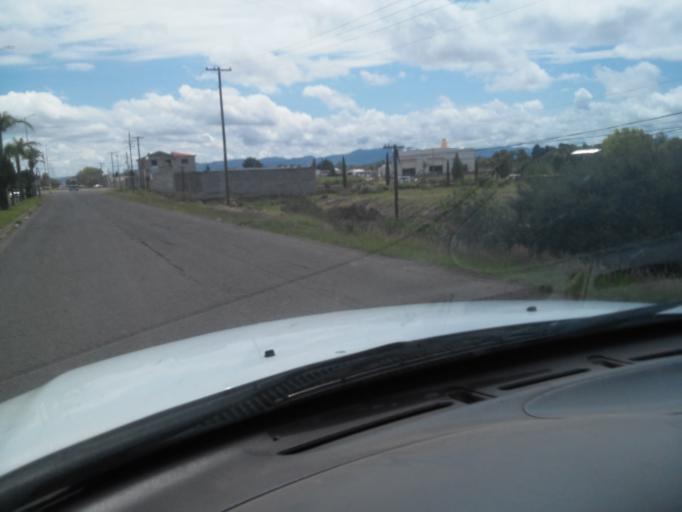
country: MX
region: Durango
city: Victoria de Durango
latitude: 24.0264
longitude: -104.5750
